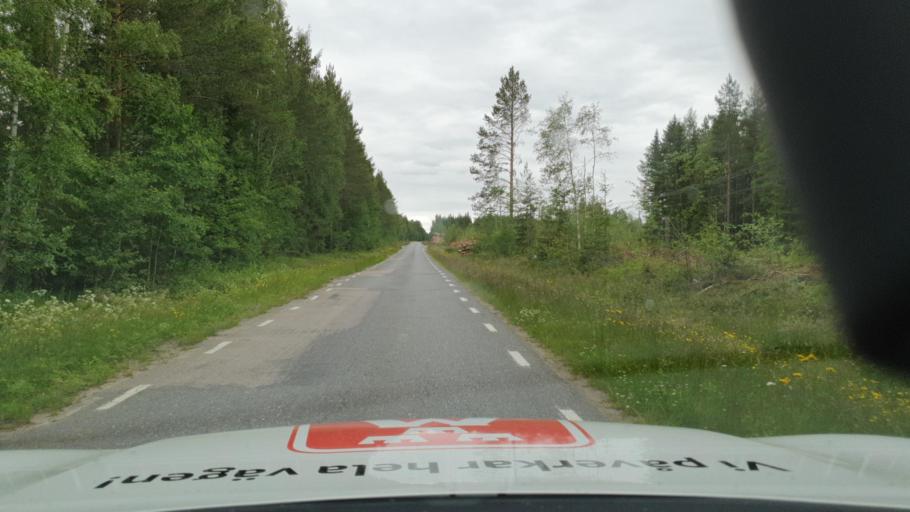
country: SE
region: Vaesterbotten
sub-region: Nordmalings Kommun
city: Nordmaling
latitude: 63.4719
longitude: 19.4623
